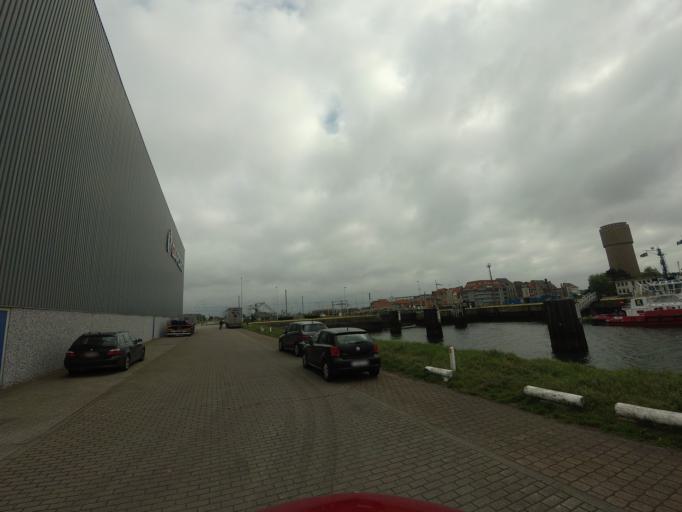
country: BE
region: Flanders
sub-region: Provincie West-Vlaanderen
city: Zeebrugge
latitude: 51.3299
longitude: 3.1986
